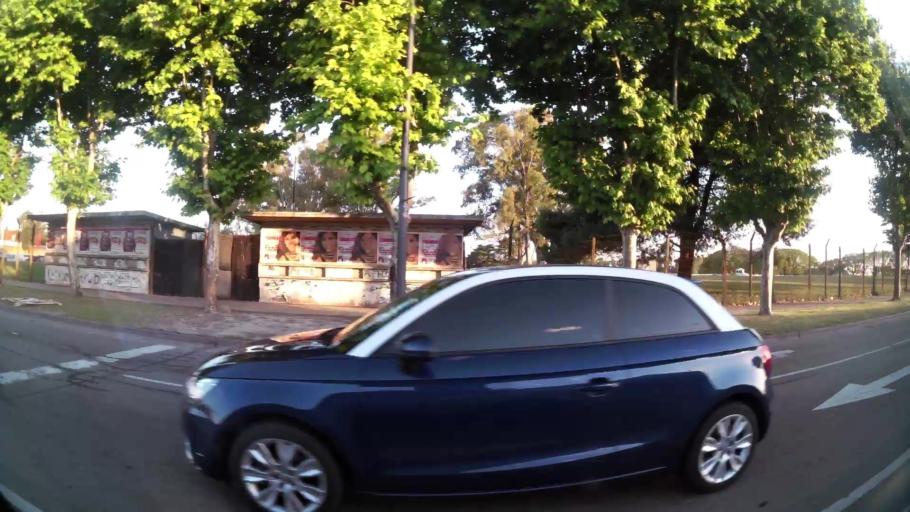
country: AR
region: Buenos Aires F.D.
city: Villa Lugano
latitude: -34.6940
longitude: -58.4655
